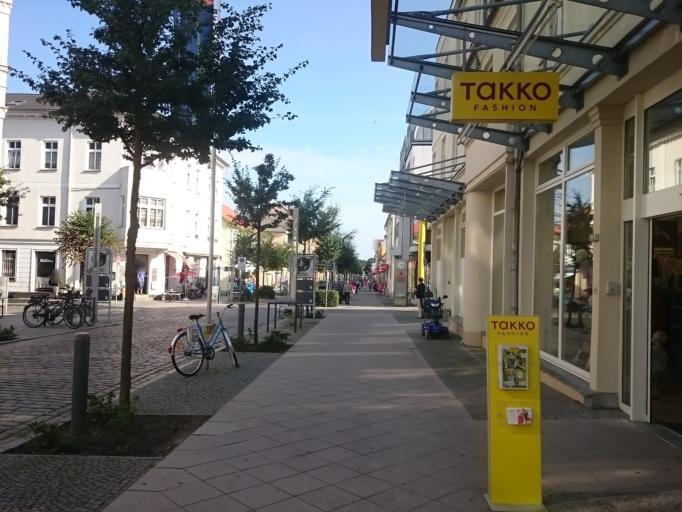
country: DE
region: Mecklenburg-Vorpommern
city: Neustrelitz
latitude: 53.3608
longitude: 13.0661
